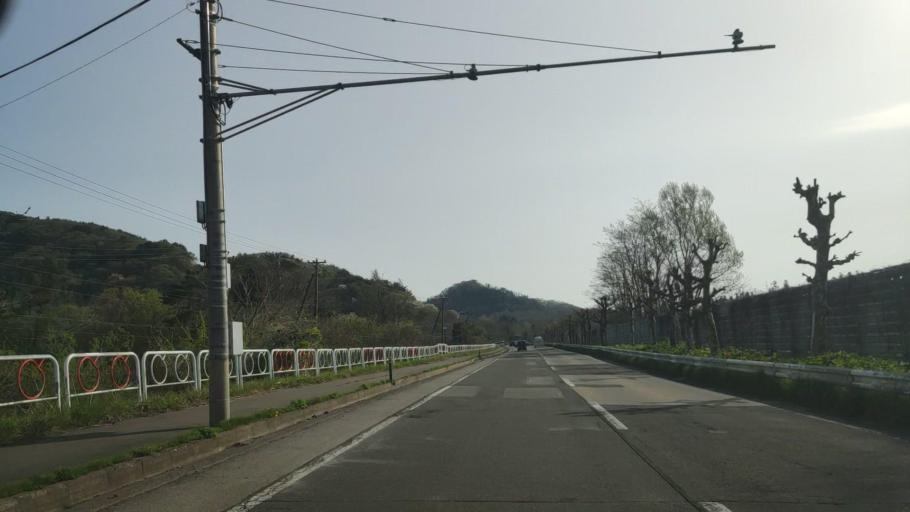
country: JP
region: Aomori
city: Aomori Shi
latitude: 40.8694
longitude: 140.8491
